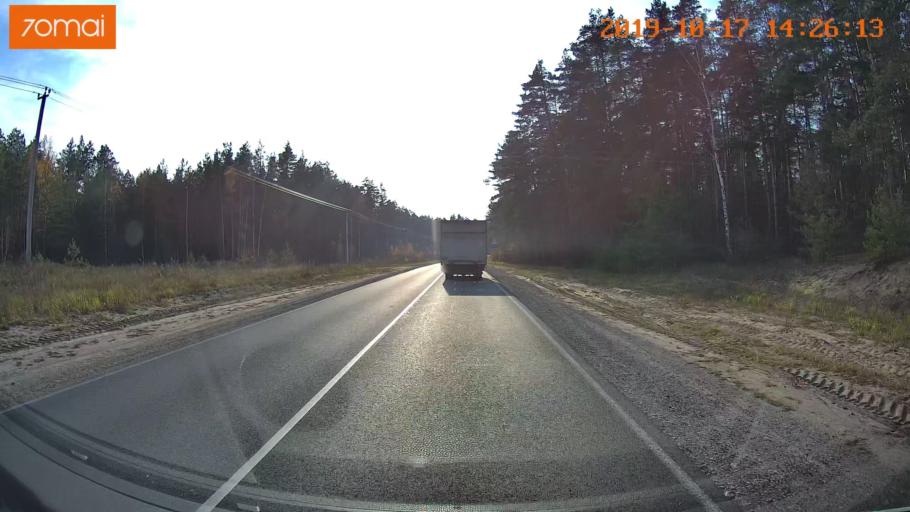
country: RU
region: Moskovskaya
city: Radovitskiy
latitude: 54.9937
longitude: 39.9697
